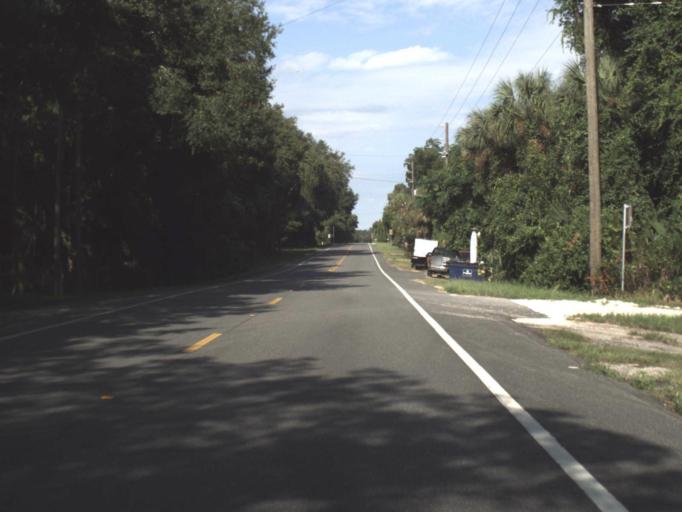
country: US
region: Florida
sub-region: Pasco County
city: Lacoochee
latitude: 28.4702
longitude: -82.1599
